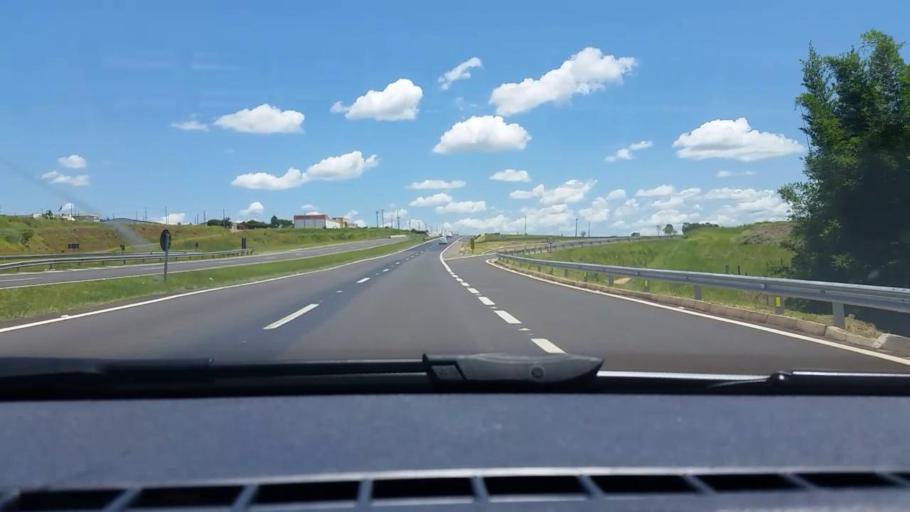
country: BR
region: Sao Paulo
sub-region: Bauru
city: Bauru
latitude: -22.4156
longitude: -49.1081
